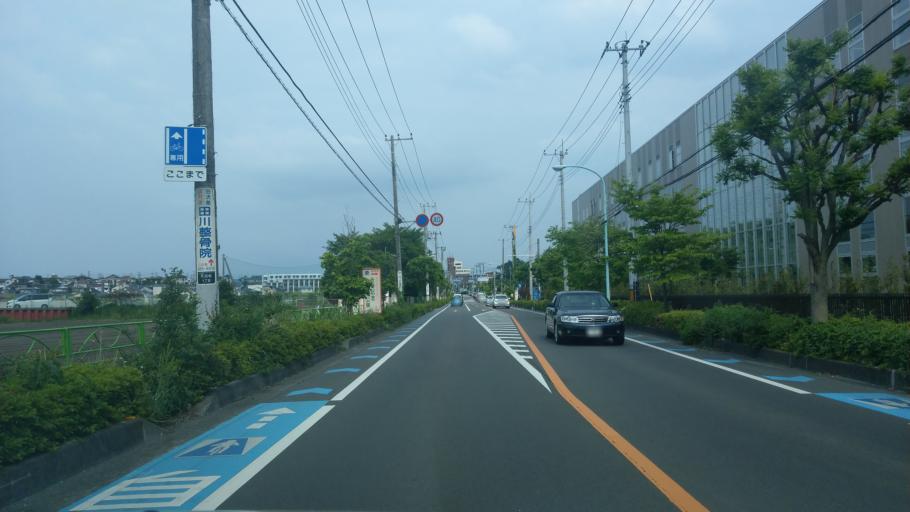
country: JP
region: Saitama
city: Saitama
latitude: 35.9080
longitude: 139.6448
